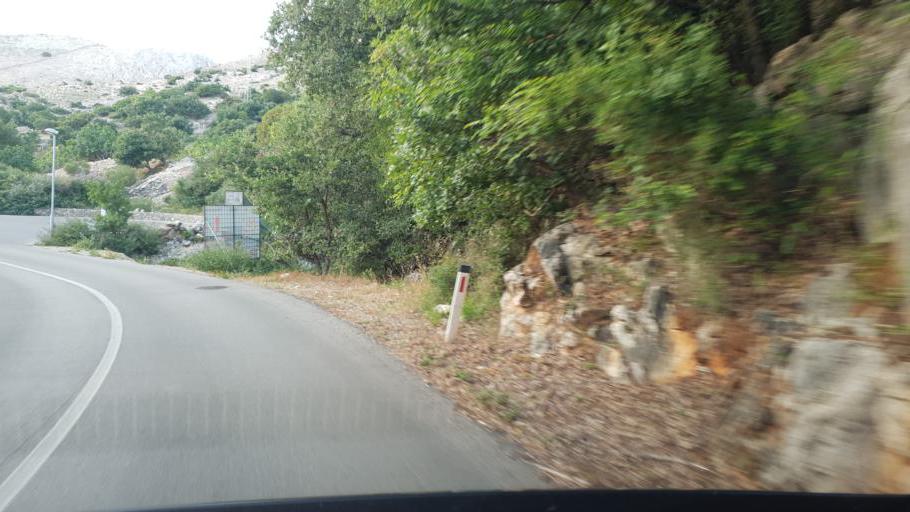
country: HR
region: Primorsko-Goranska
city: Punat
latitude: 44.9649
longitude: 14.6800
